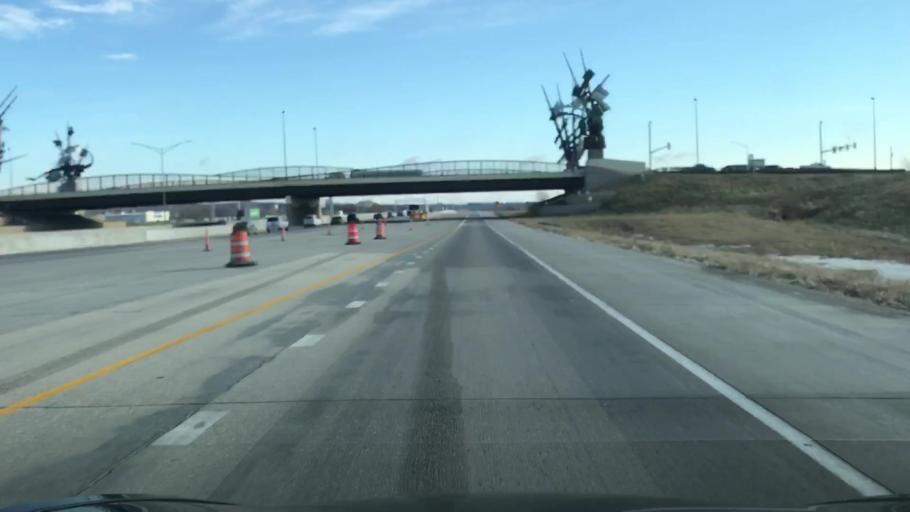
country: US
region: Iowa
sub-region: Pottawattamie County
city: Council Bluffs
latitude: 41.2321
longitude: -95.8812
